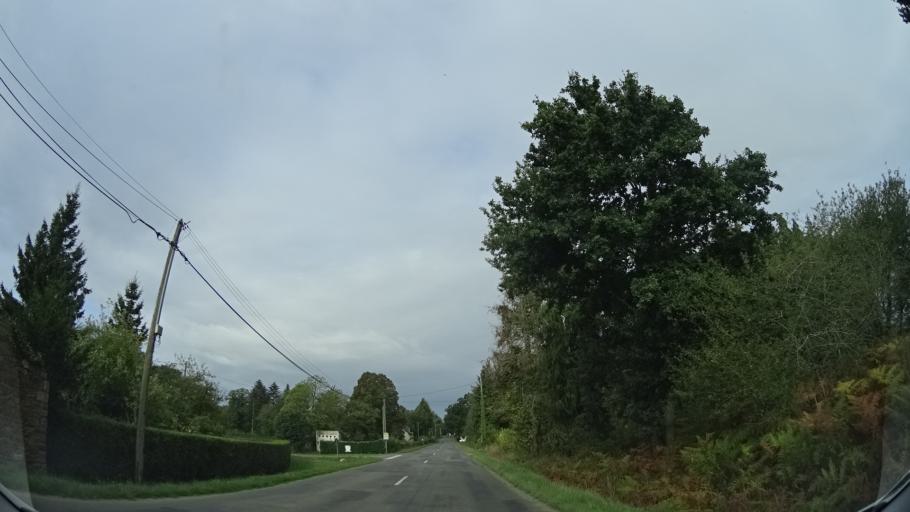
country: FR
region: Brittany
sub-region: Departement d'Ille-et-Vilaine
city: Guipel
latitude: 48.2991
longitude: -1.7426
